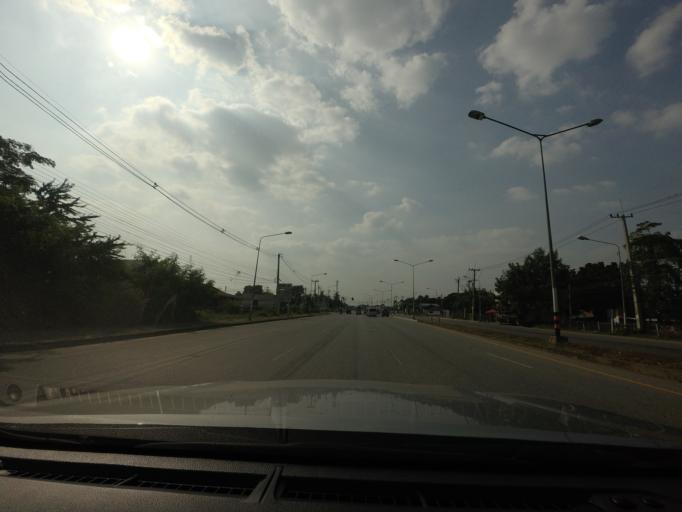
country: TH
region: Sukhothai
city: Sukhothai
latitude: 17.0261
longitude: 99.8831
